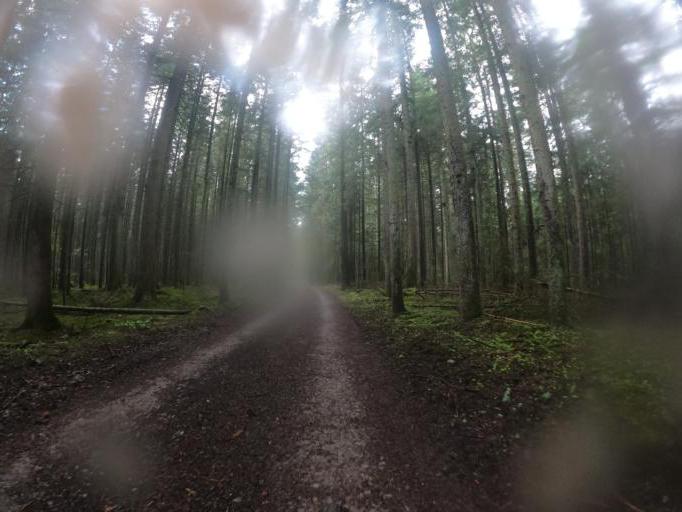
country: DE
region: Baden-Wuerttemberg
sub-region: Karlsruhe Region
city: Oberreichenbach
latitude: 48.7051
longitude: 8.6342
